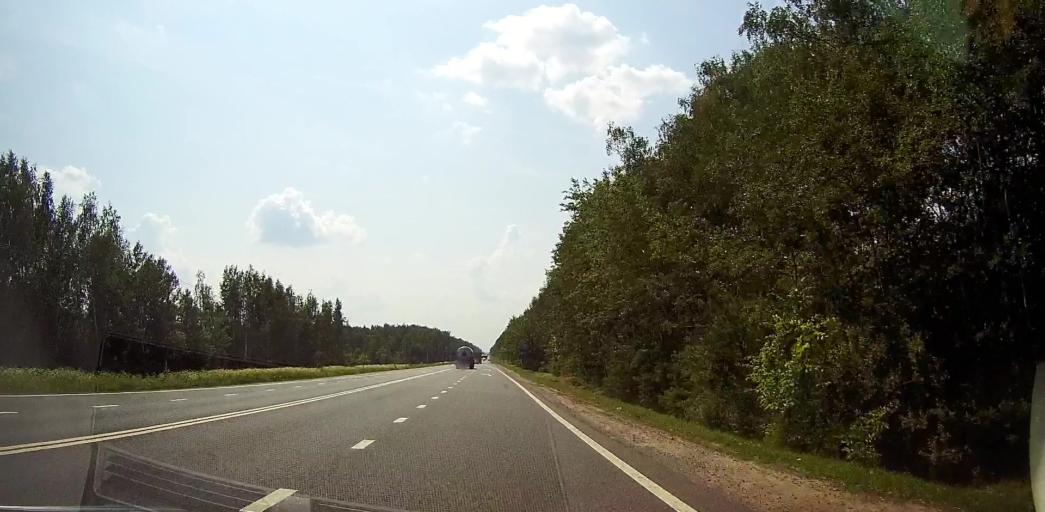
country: RU
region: Moskovskaya
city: Meshcherino
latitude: 55.2219
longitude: 38.4000
